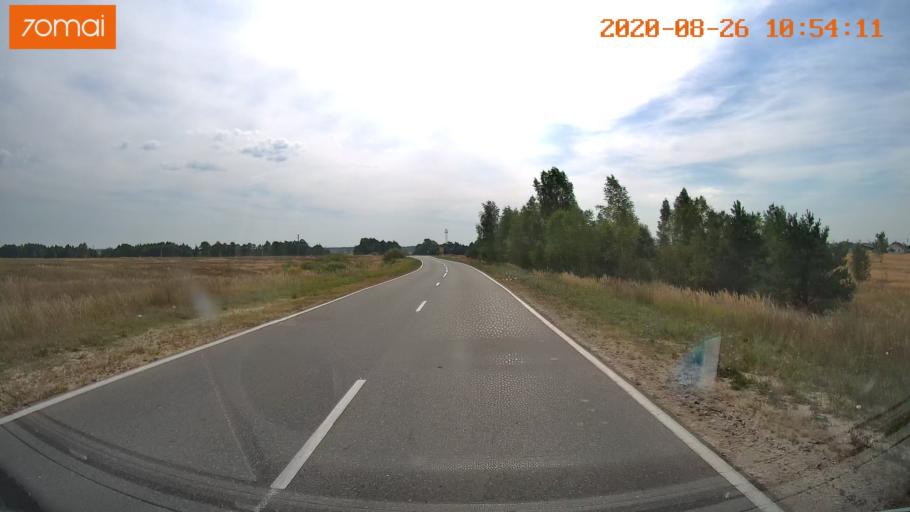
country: RU
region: Rjazan
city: Izhevskoye
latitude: 54.6312
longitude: 41.1575
